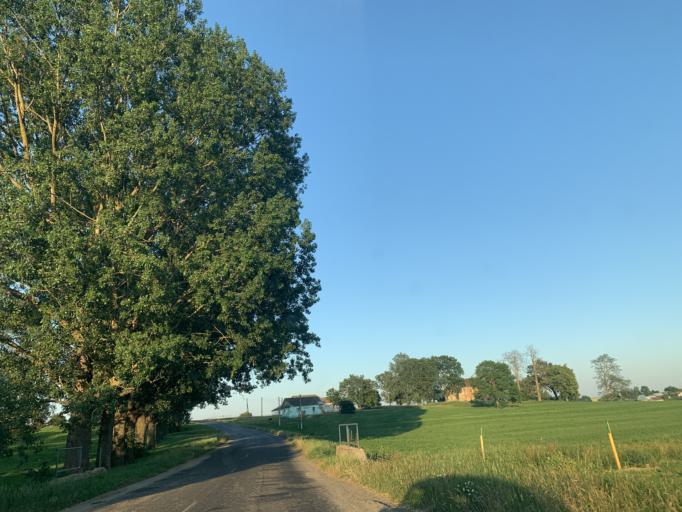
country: BY
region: Minsk
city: Haradzyeya
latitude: 53.2431
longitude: 26.5015
